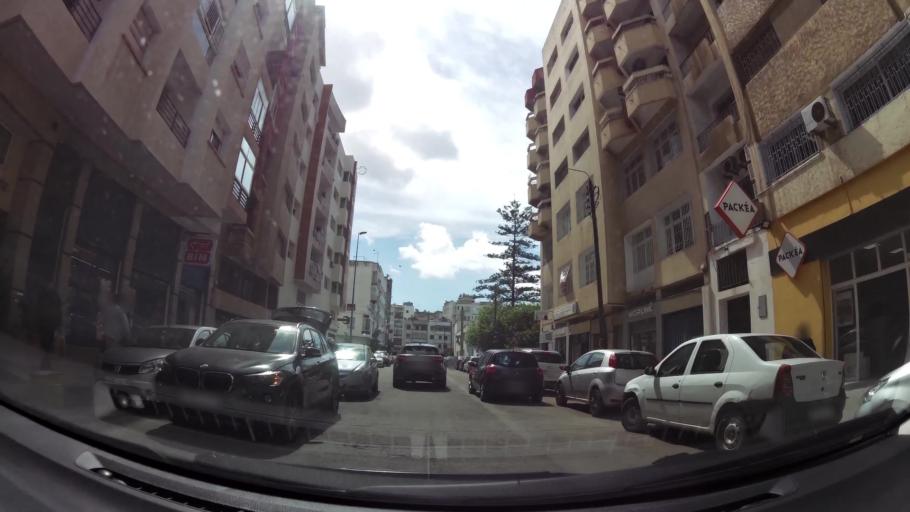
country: MA
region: Grand Casablanca
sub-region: Casablanca
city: Casablanca
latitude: 33.5782
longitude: -7.6399
